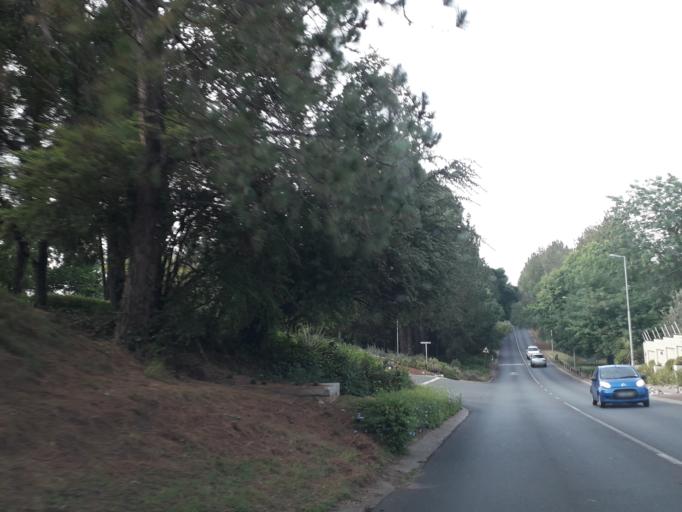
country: ZA
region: Gauteng
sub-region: City of Johannesburg Metropolitan Municipality
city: Johannesburg
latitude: -26.0811
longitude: 28.0425
